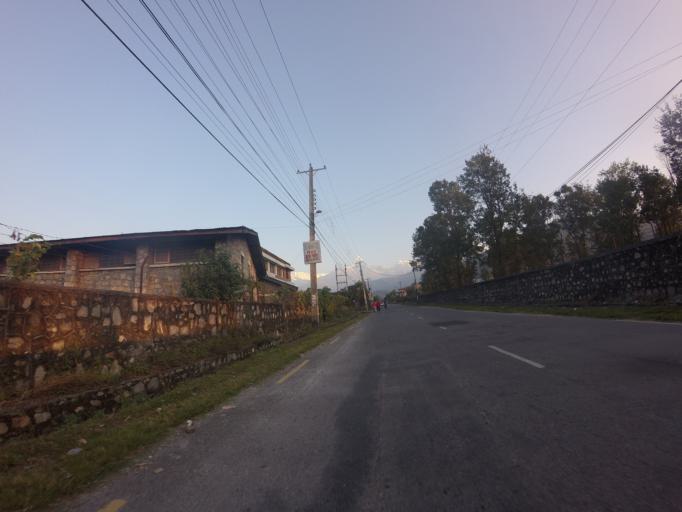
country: NP
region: Western Region
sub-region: Gandaki Zone
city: Pokhara
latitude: 28.2149
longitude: 83.9980
